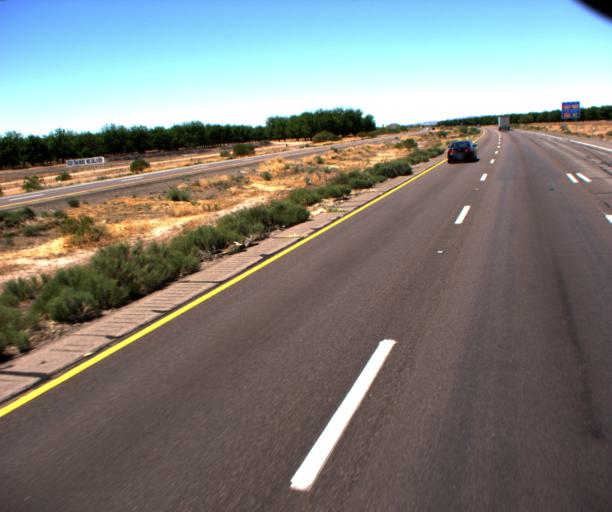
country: US
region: Arizona
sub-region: Pinal County
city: Eloy
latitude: 32.7259
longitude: -111.5200
